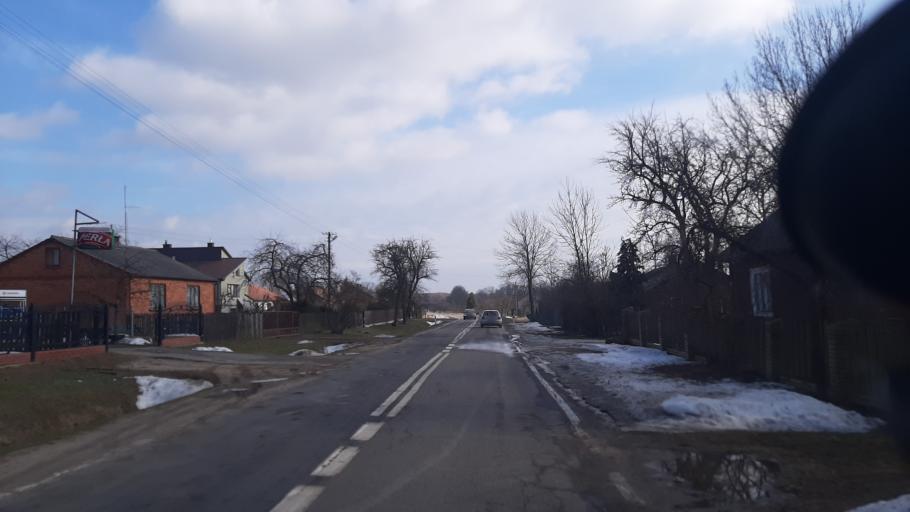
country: PL
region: Lublin Voivodeship
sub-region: Powiat parczewski
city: Sosnowica
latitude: 51.4988
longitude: 23.1608
